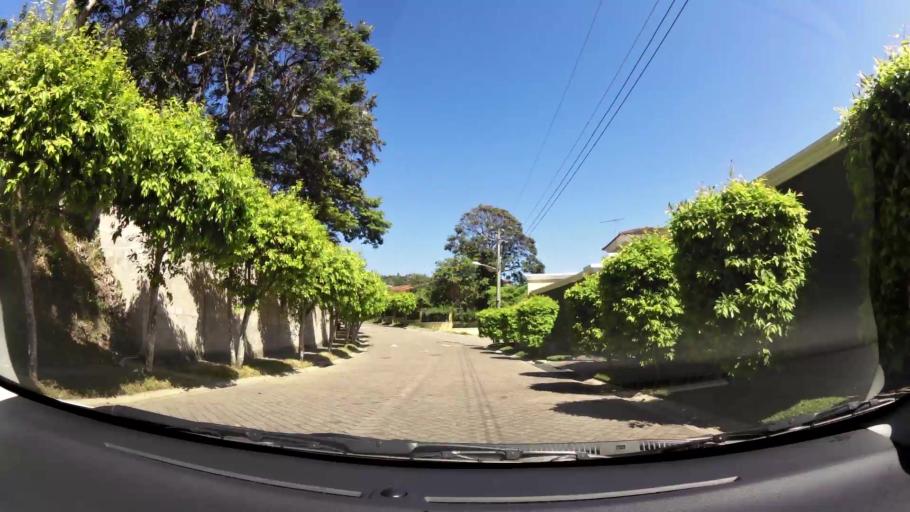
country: SV
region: La Libertad
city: Nuevo Cuscatlan
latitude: 13.6569
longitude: -89.2823
